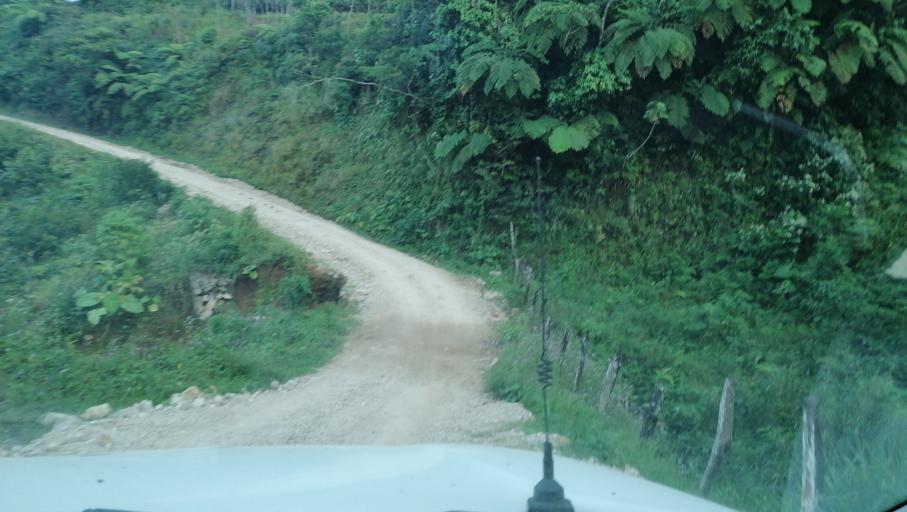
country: MX
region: Chiapas
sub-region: Francisco Leon
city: San Miguel la Sardina
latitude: 17.3004
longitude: -93.2651
